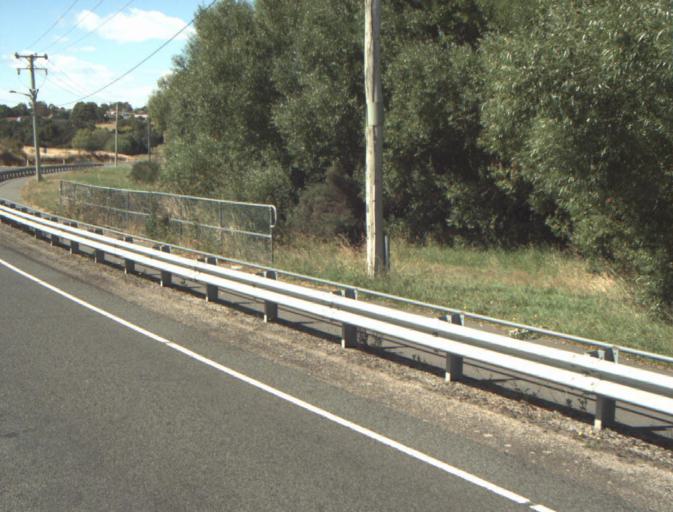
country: AU
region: Tasmania
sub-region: Launceston
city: Newstead
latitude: -41.4258
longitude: 147.1857
